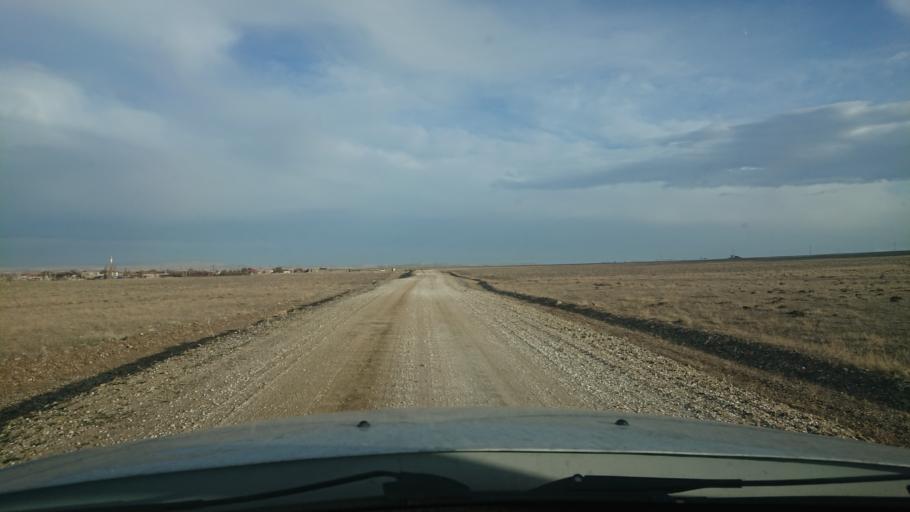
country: TR
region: Aksaray
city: Agacoren
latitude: 38.7099
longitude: 33.8684
